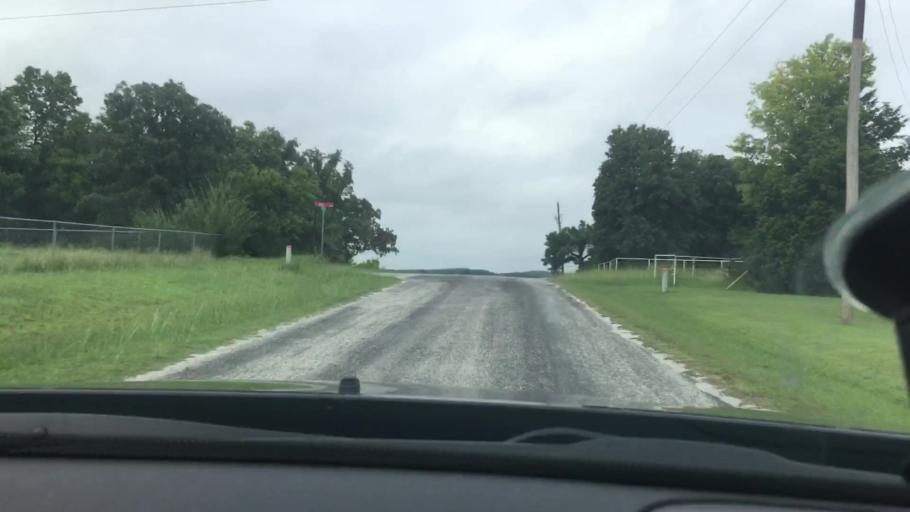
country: US
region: Oklahoma
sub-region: Pontotoc County
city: Byng
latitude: 34.8094
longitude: -96.5475
